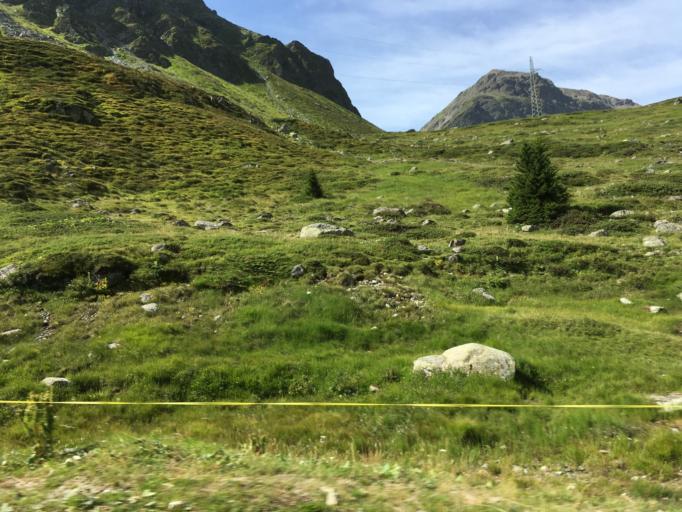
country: CH
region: Grisons
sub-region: Maloja District
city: Silvaplana
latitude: 46.4642
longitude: 9.7005
